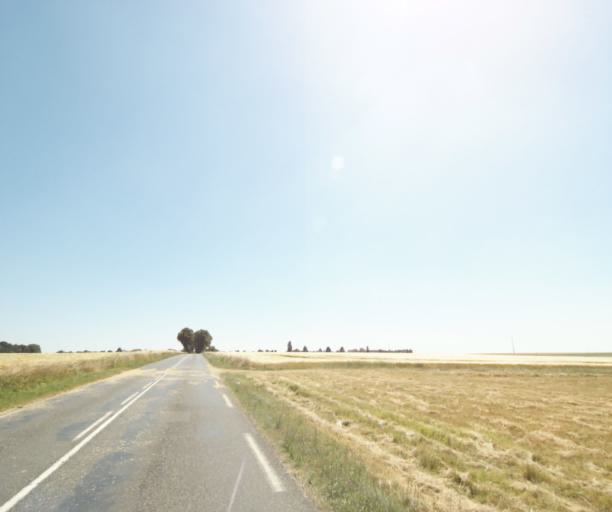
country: FR
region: Ile-de-France
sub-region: Departement de l'Essonne
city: Milly-la-Foret
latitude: 48.3522
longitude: 2.4551
